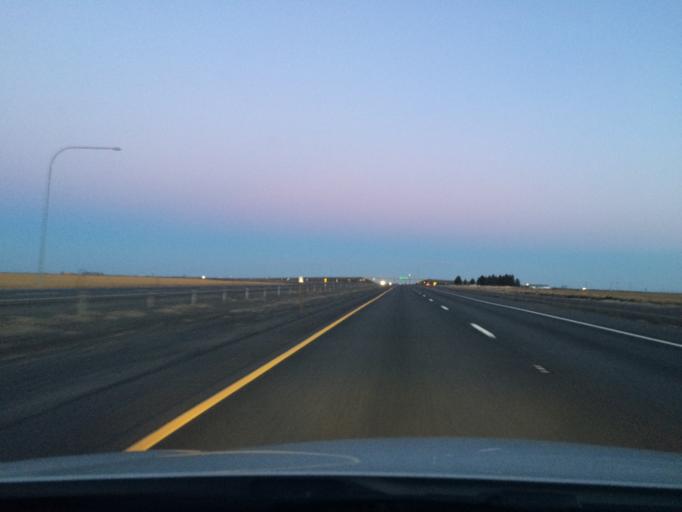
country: US
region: Washington
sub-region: Grant County
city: Quincy
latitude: 47.1035
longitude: -119.7778
